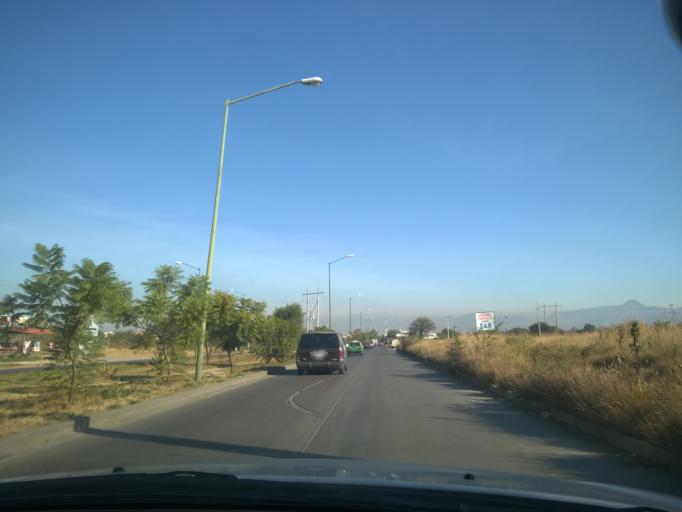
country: MX
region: Guanajuato
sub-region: Leon
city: San Jose de Duran (Los Troncoso)
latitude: 21.0900
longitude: -101.6424
